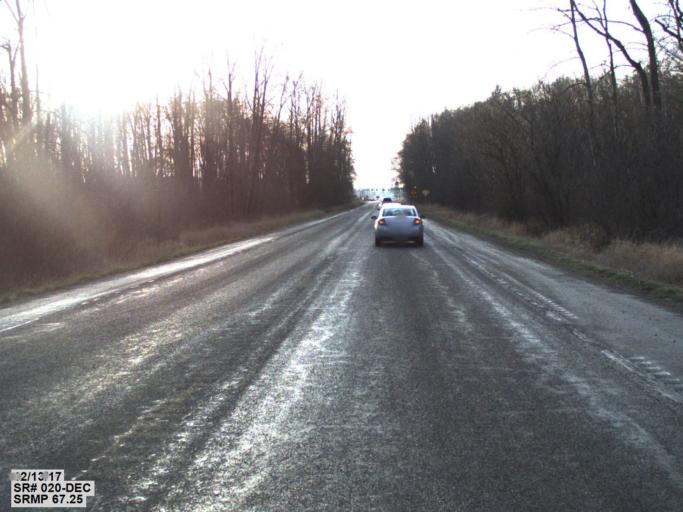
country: US
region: Washington
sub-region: Skagit County
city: Sedro-Woolley
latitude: 48.5189
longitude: -122.2041
